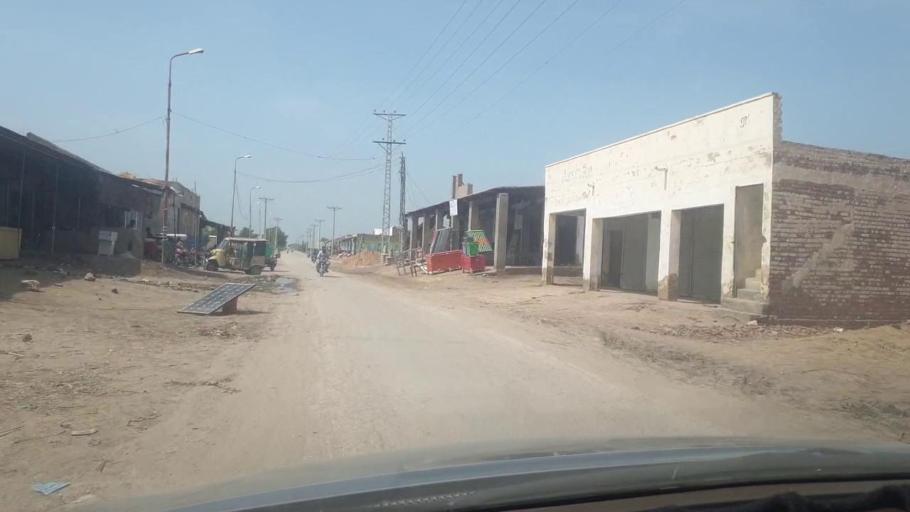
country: PK
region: Sindh
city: Gambat
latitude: 27.2979
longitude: 68.6098
